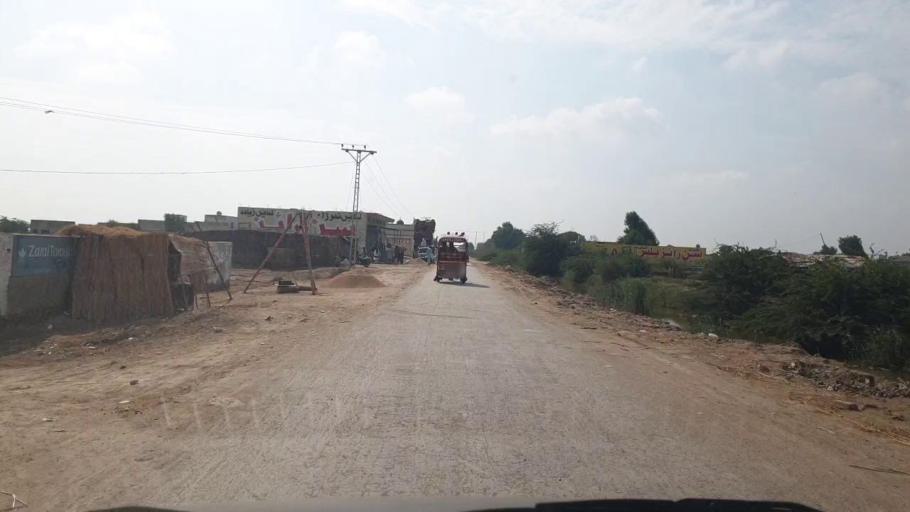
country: PK
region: Sindh
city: Kario
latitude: 24.6533
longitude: 68.5423
